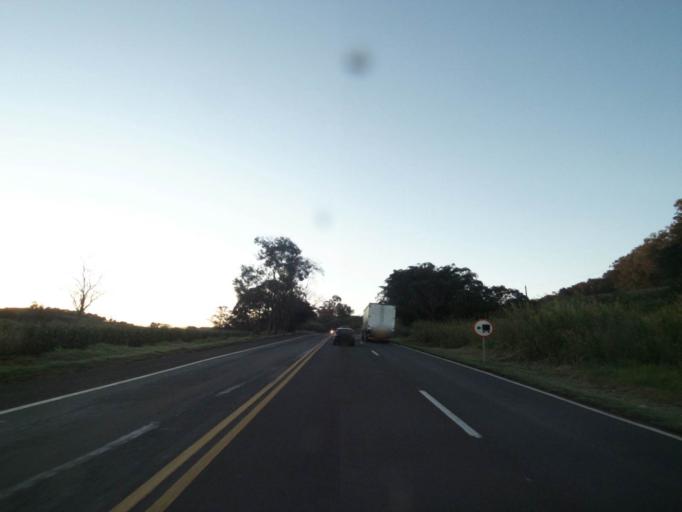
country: BR
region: Parana
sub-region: Londrina
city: Londrina
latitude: -23.4460
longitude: -51.1335
